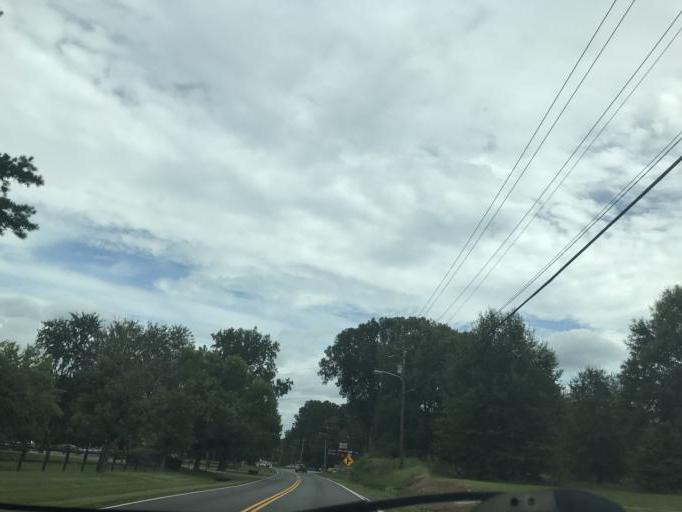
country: US
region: South Carolina
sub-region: Cherokee County
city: Gaffney
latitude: 35.0915
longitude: -81.6531
